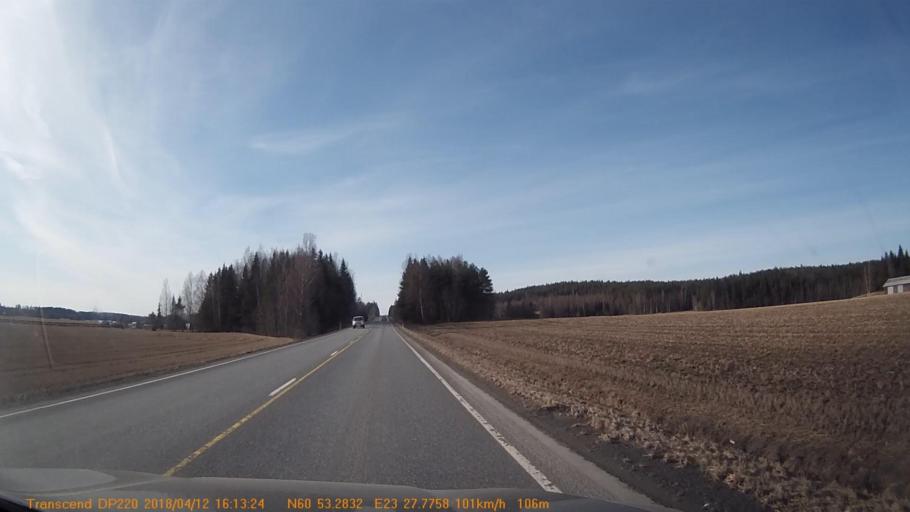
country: FI
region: Haeme
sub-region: Forssa
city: Jokioinen
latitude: 60.8883
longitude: 23.4625
